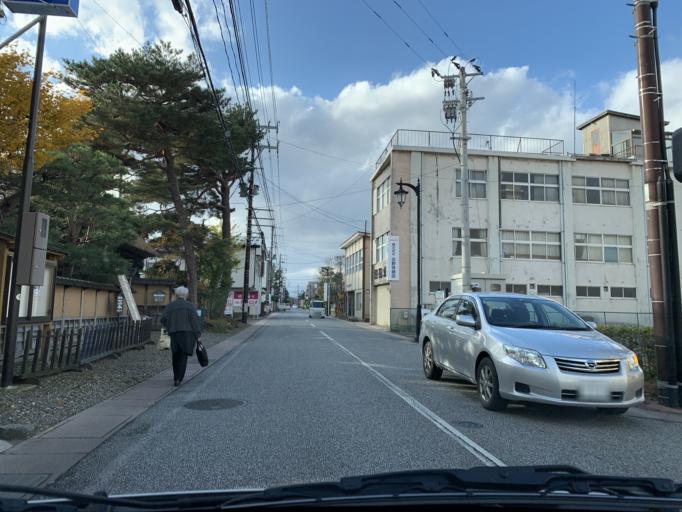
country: JP
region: Iwate
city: Mizusawa
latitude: 39.1431
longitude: 141.1394
